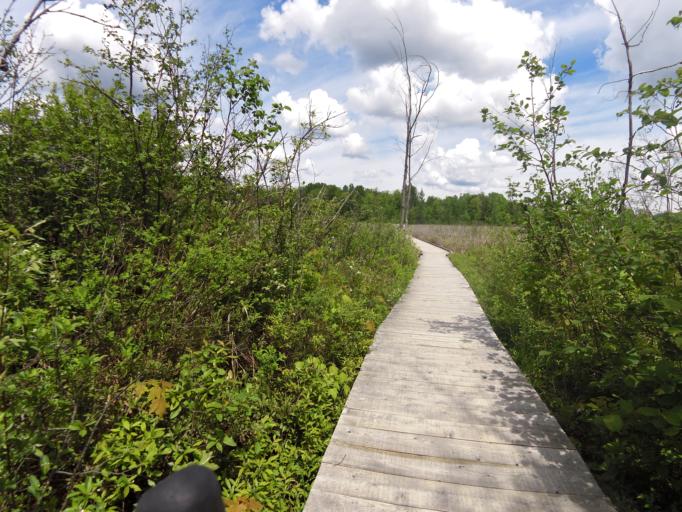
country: CA
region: Ontario
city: Ottawa
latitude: 45.3915
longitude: -75.5092
